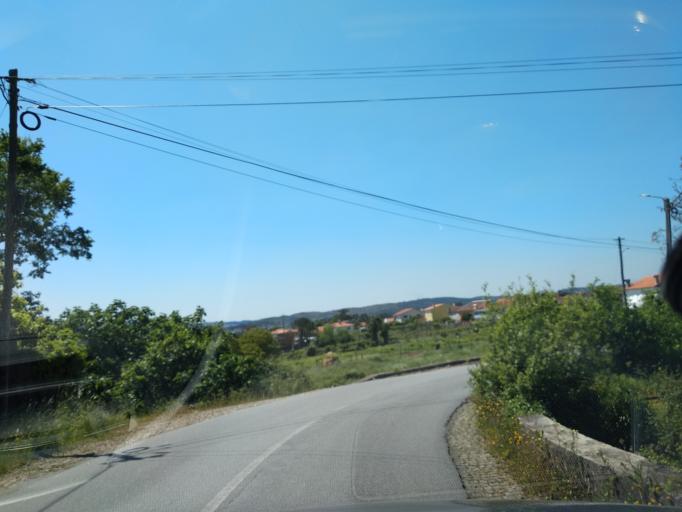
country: PT
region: Porto
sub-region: Paredes
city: Gandra
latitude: 41.1849
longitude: -8.4256
